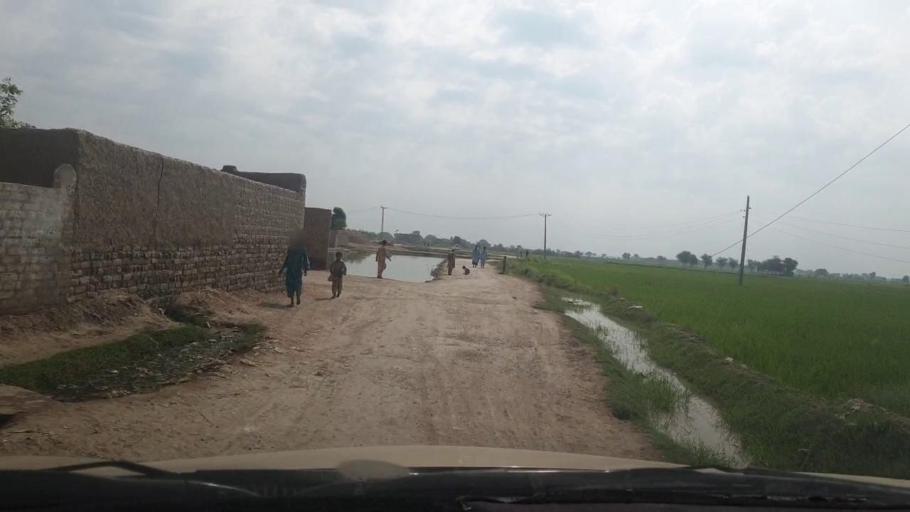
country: PK
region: Sindh
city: Larkana
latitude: 27.6516
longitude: 68.1984
